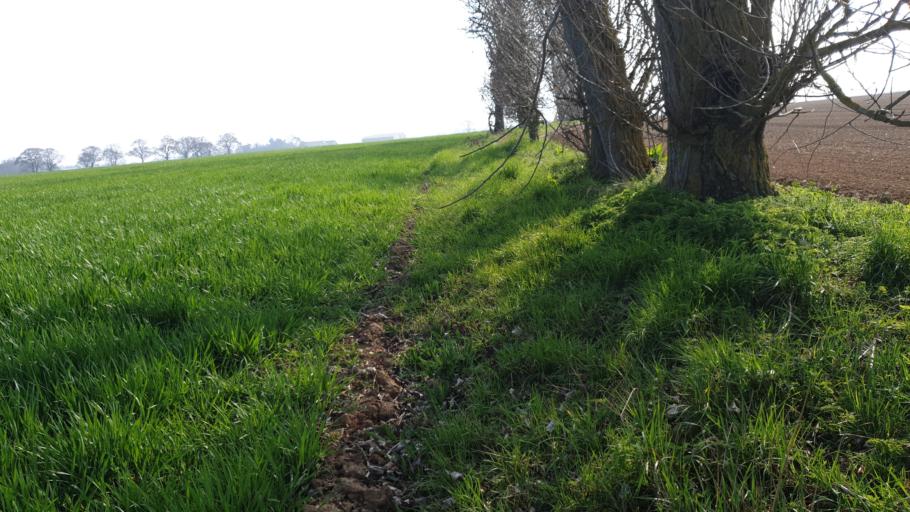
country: GB
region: England
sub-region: Essex
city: Mistley
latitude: 51.8973
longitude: 1.1228
